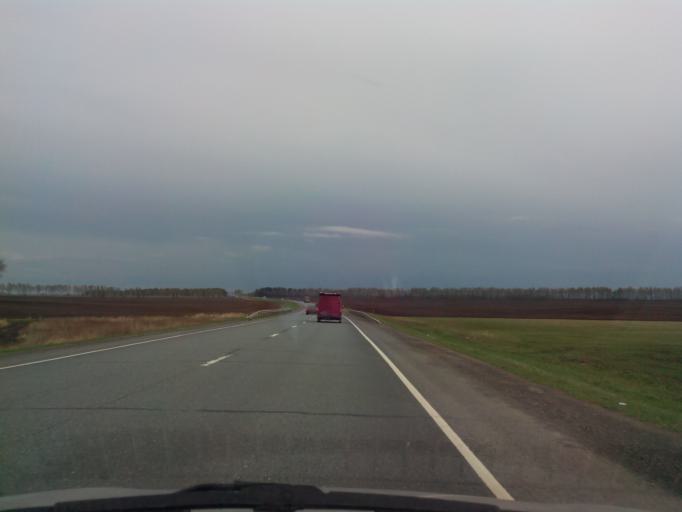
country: RU
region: Moskovskaya
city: Uzunovo
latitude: 54.6077
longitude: 38.4034
